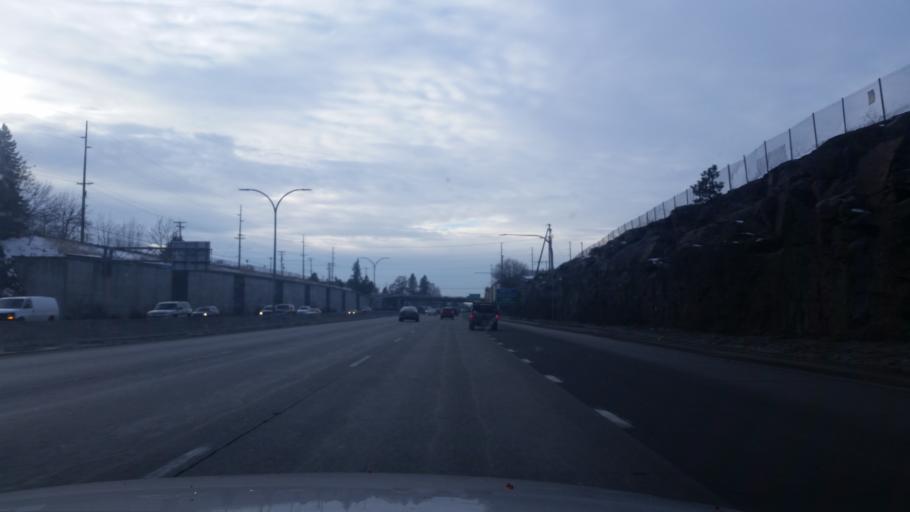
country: US
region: Washington
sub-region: Spokane County
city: Spokane
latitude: 47.6524
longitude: -117.3977
